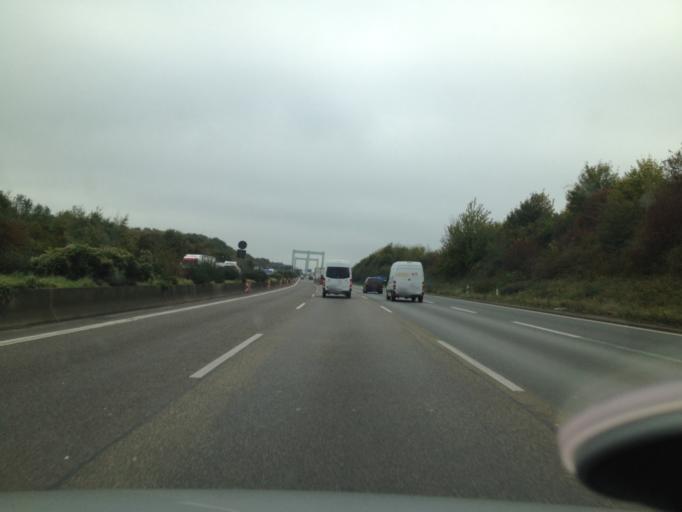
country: DE
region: North Rhine-Westphalia
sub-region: Regierungsbezirk Koln
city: Poll
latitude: 50.9092
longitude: 7.0018
